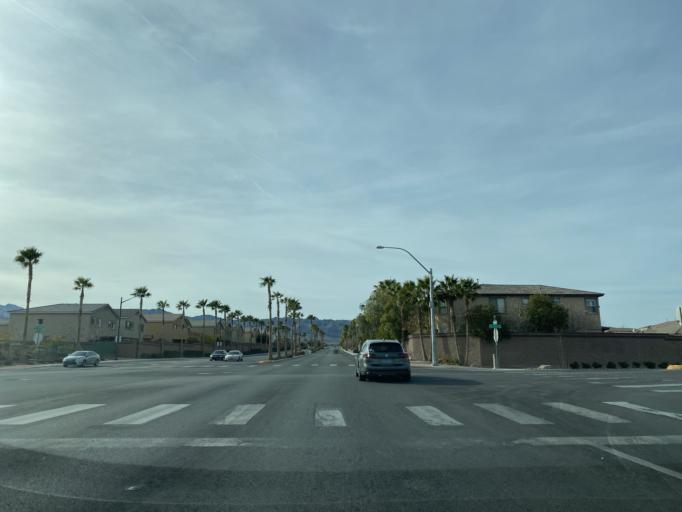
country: US
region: Nevada
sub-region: Clark County
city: Summerlin South
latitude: 36.2919
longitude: -115.2966
